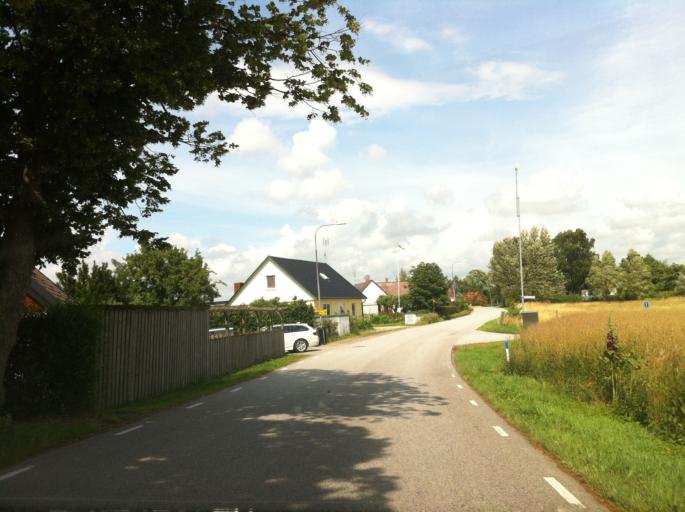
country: SE
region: Skane
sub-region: Skurups Kommun
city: Skurup
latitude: 55.4567
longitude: 13.4288
